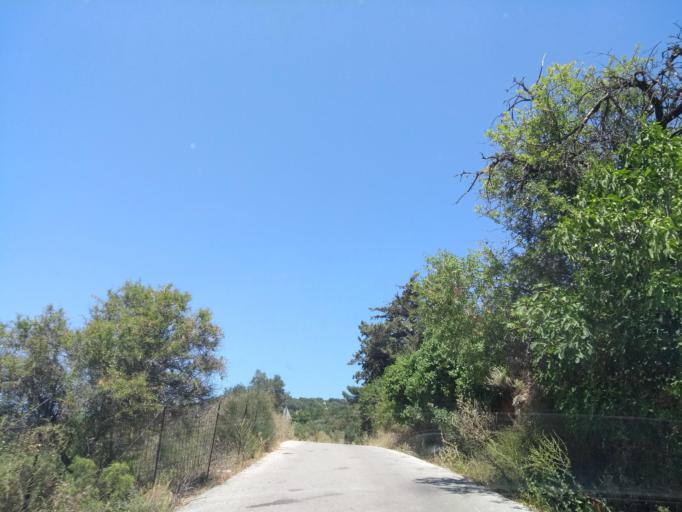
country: GR
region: Crete
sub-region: Nomos Chanias
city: Georgioupolis
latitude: 35.3192
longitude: 24.3089
